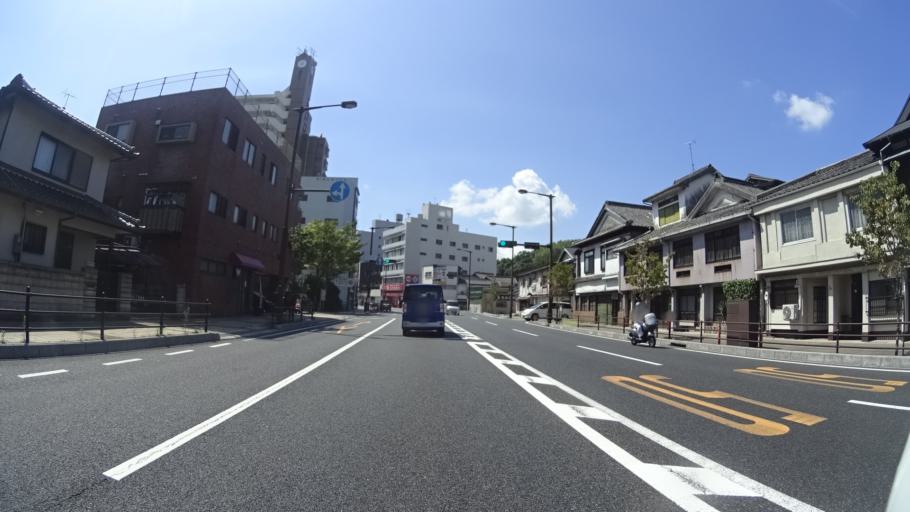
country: JP
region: Yamaguchi
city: Shimonoseki
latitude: 33.9568
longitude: 130.9209
